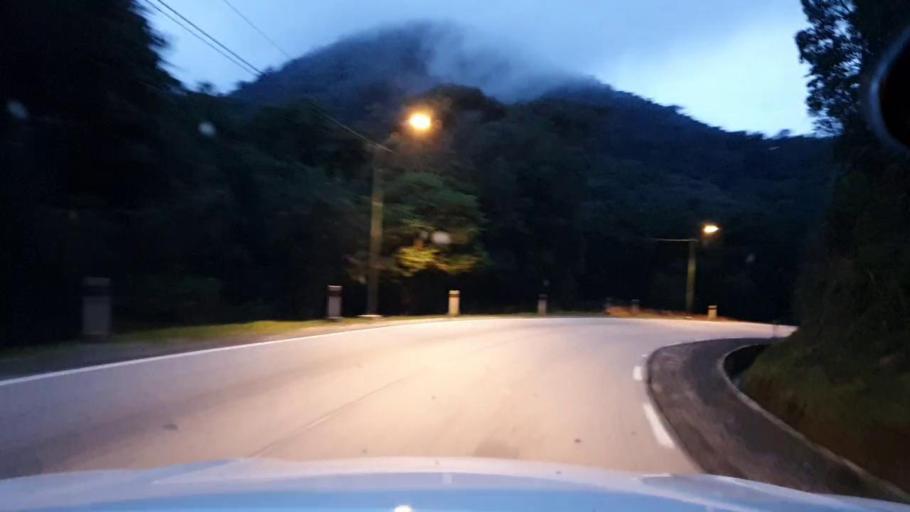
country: RW
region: Southern Province
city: Nzega
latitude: -2.5288
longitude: 29.3811
